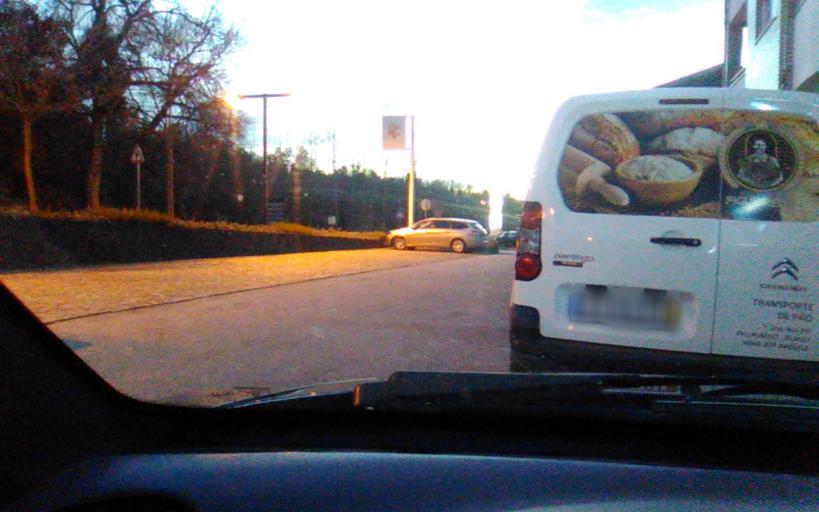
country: PT
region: Aveiro
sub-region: Arouca
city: Arouca
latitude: 40.9279
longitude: -8.2554
